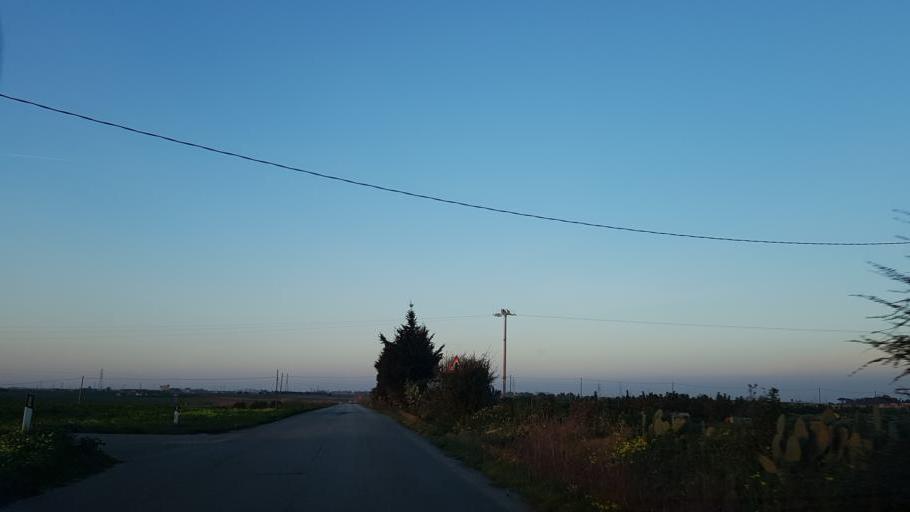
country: IT
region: Apulia
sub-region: Provincia di Brindisi
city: Tuturano
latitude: 40.5747
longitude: 17.9496
